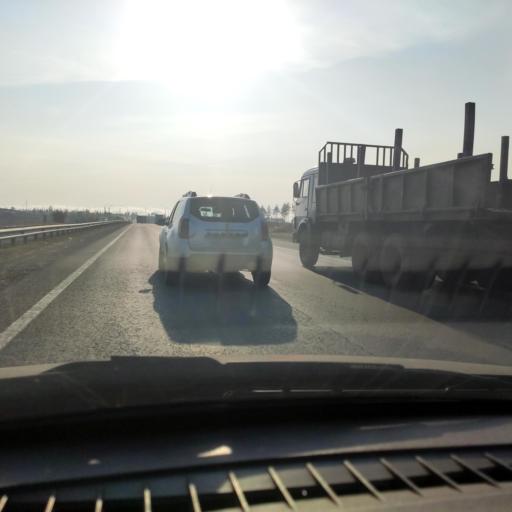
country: RU
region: Samara
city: Zhigulevsk
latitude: 53.5068
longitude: 49.5382
